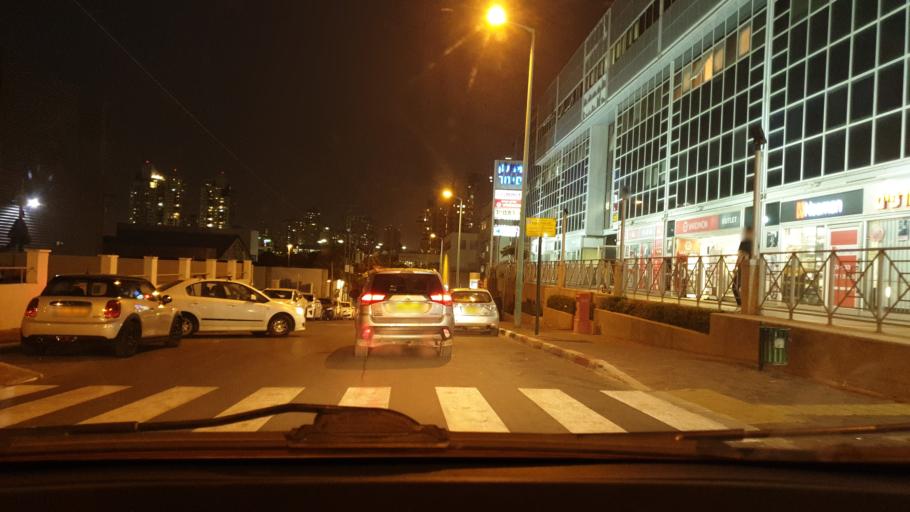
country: IL
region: Tel Aviv
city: Giv`at Shemu'el
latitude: 32.0876
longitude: 34.8535
